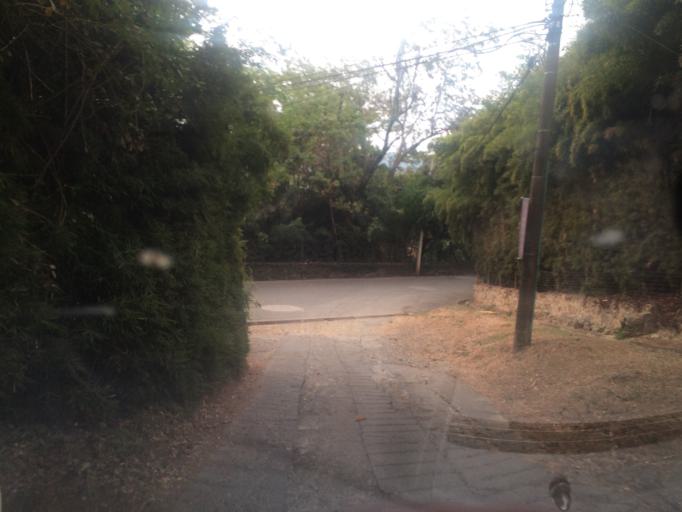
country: CO
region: Valle del Cauca
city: Cali
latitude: 3.4407
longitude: -76.5563
